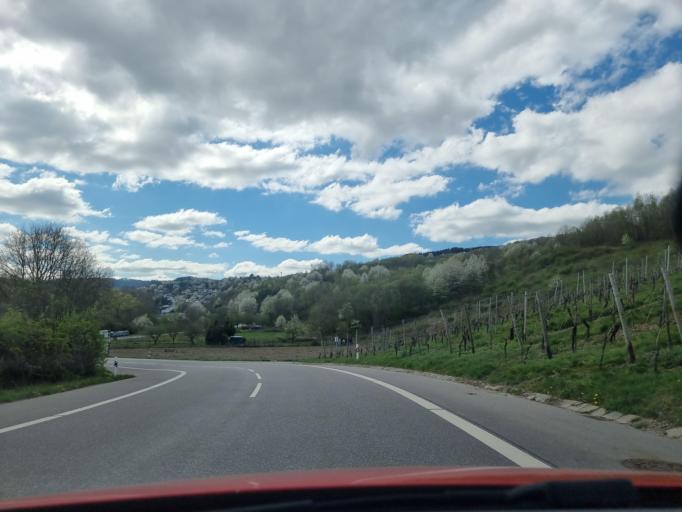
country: DE
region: Rheinland-Pfalz
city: Fell
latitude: 49.7832
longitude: 6.7722
